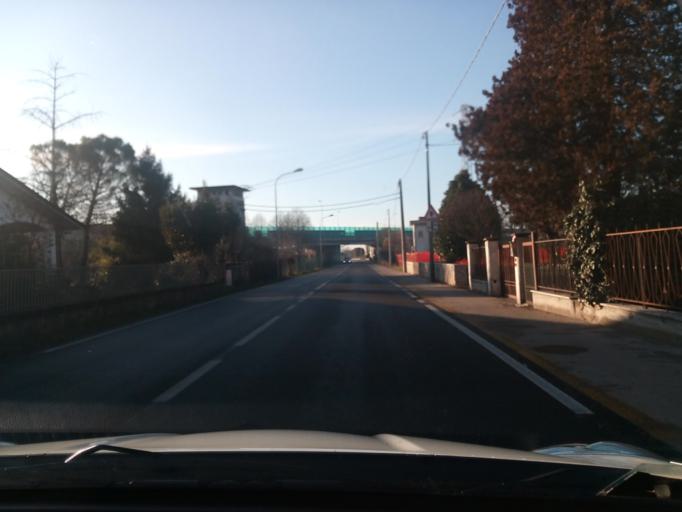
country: IT
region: Veneto
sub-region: Provincia di Vicenza
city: Dueville
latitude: 45.6430
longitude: 11.5677
